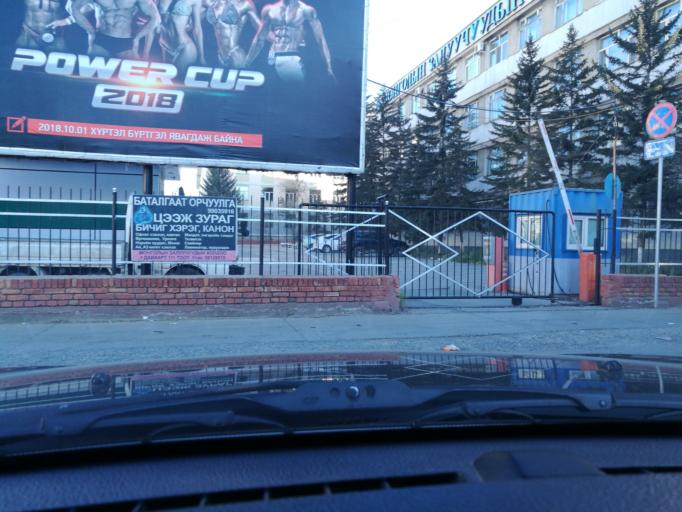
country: MN
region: Ulaanbaatar
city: Ulaanbaatar
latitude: 47.9209
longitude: 106.9236
